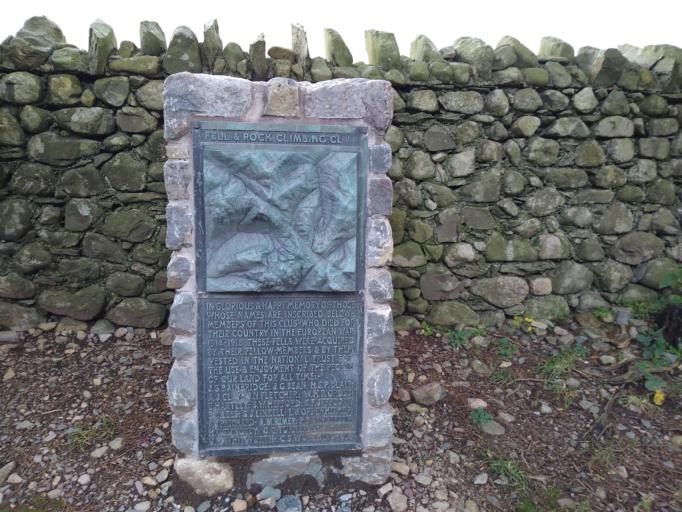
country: GB
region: England
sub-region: Cumbria
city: Keswick
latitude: 54.4671
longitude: -3.2534
